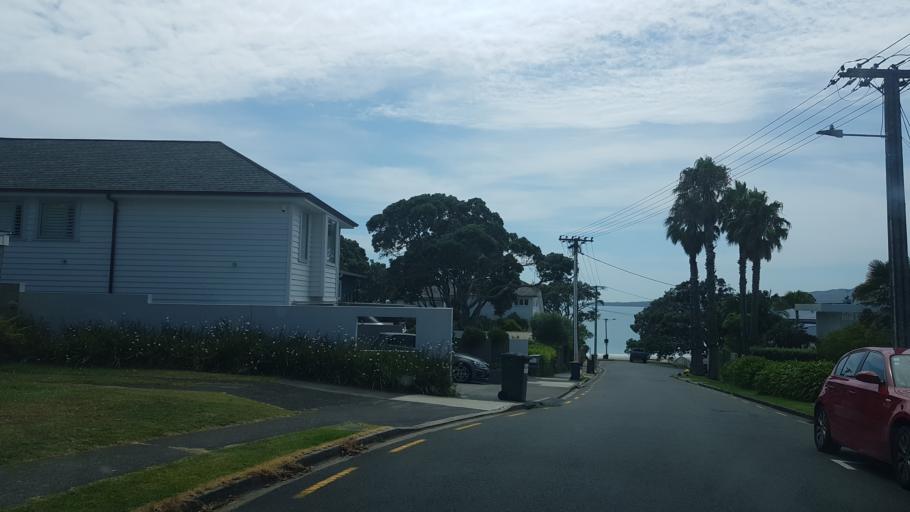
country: NZ
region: Auckland
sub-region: Auckland
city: North Shore
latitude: -36.7916
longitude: 174.7772
